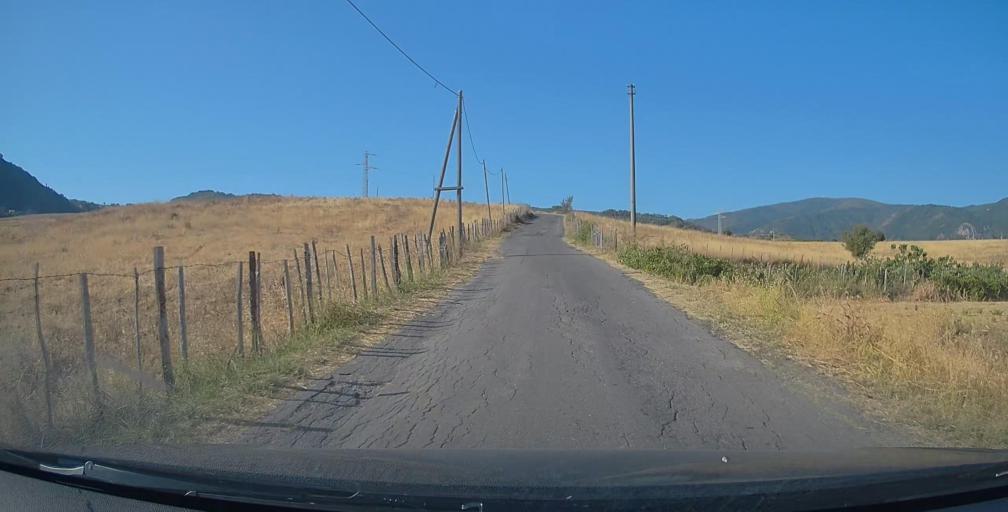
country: IT
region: Sicily
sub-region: Messina
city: San Piero Patti
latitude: 38.0730
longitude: 14.9855
